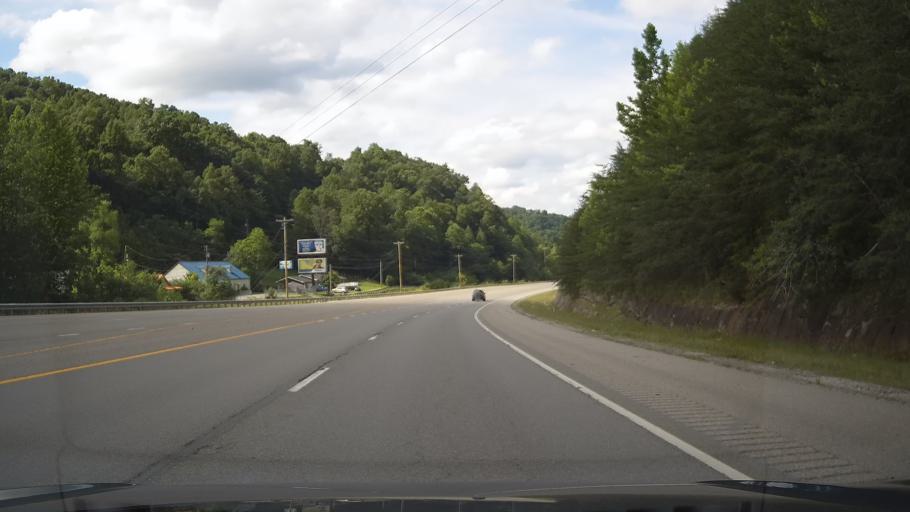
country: US
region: Kentucky
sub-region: Floyd County
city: Prestonsburg
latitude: 37.7089
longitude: -82.7939
